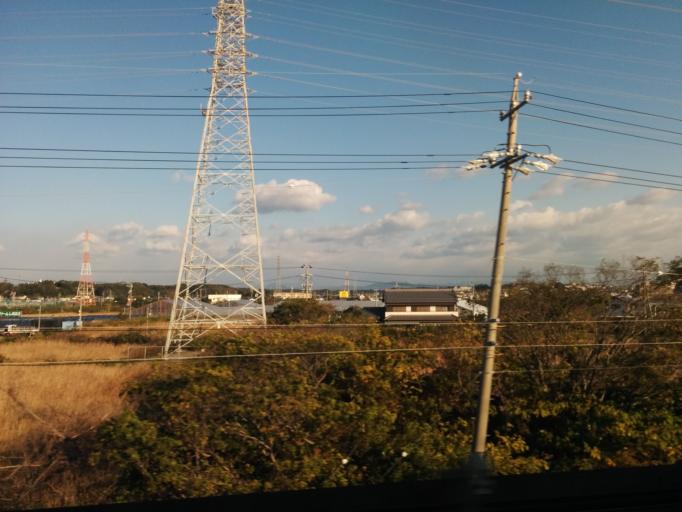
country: JP
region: Shizuoka
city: Hamamatsu
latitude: 34.6933
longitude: 137.6694
